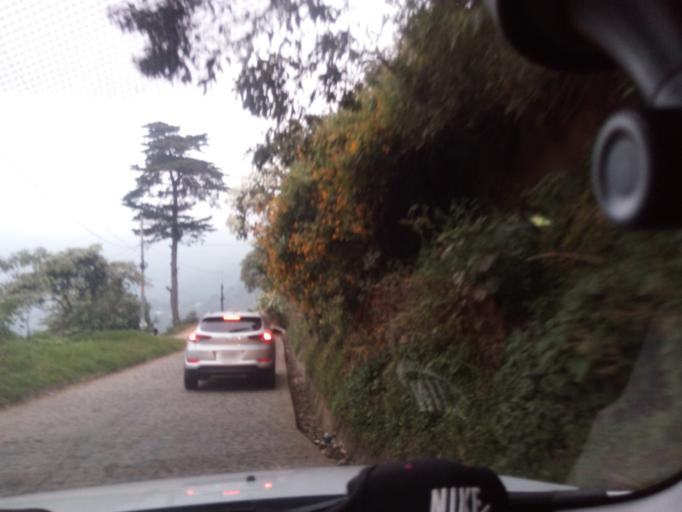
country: GT
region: Sacatepequez
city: Antigua Guatemala
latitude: 14.5828
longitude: -90.7110
